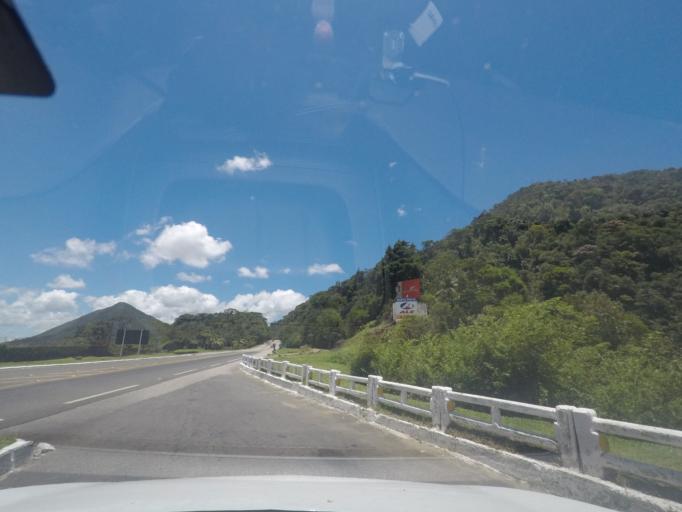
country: BR
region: Rio de Janeiro
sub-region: Teresopolis
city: Teresopolis
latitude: -22.4625
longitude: -42.9864
